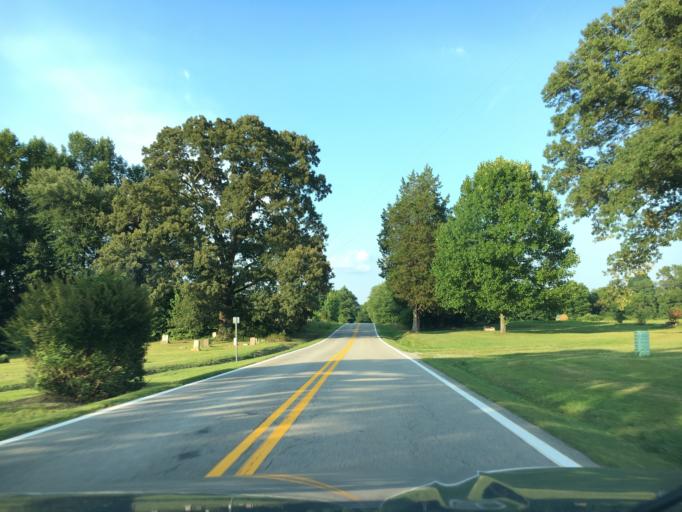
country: US
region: Virginia
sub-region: Pittsylvania County
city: Chatham
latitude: 36.8203
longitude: -79.2562
